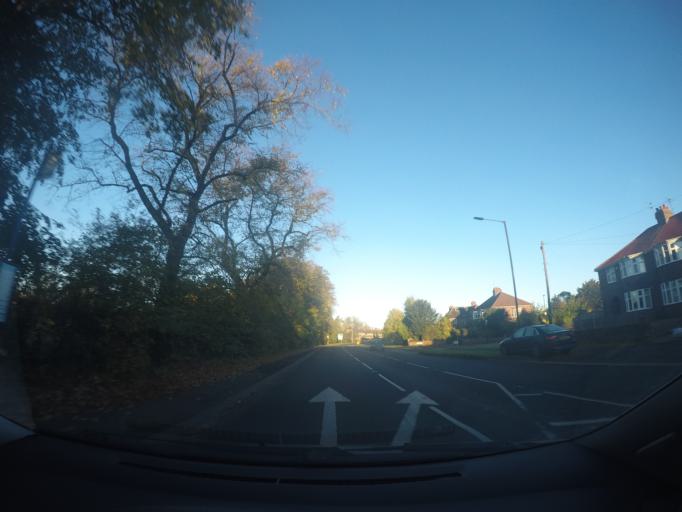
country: GB
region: England
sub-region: City of York
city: Skelton
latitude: 53.9797
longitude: -1.1136
